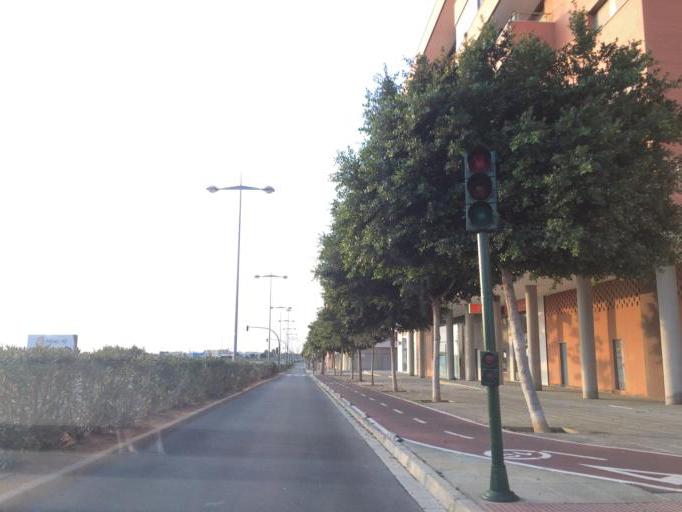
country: ES
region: Andalusia
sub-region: Provincia de Almeria
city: Almeria
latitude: 36.8352
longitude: -2.4385
